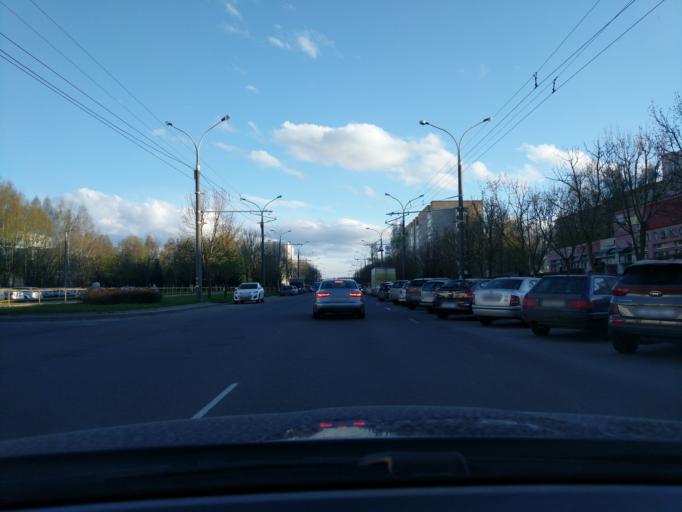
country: BY
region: Minsk
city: Novoye Medvezhino
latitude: 53.8978
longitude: 27.4529
